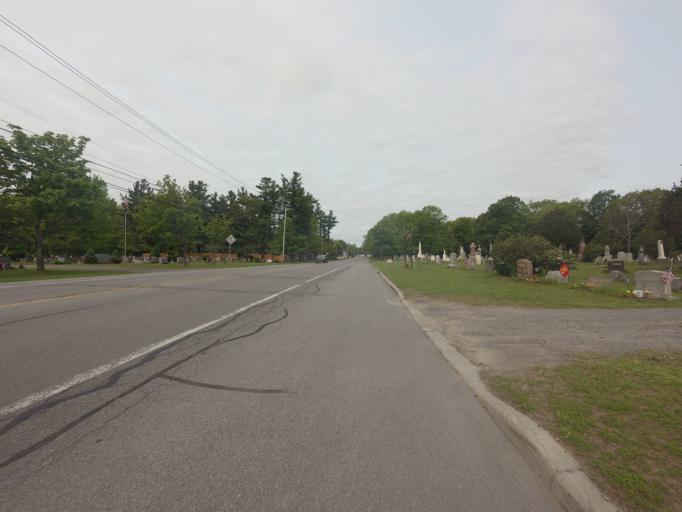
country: US
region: New York
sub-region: Jefferson County
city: Black River
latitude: 44.0071
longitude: -75.7837
